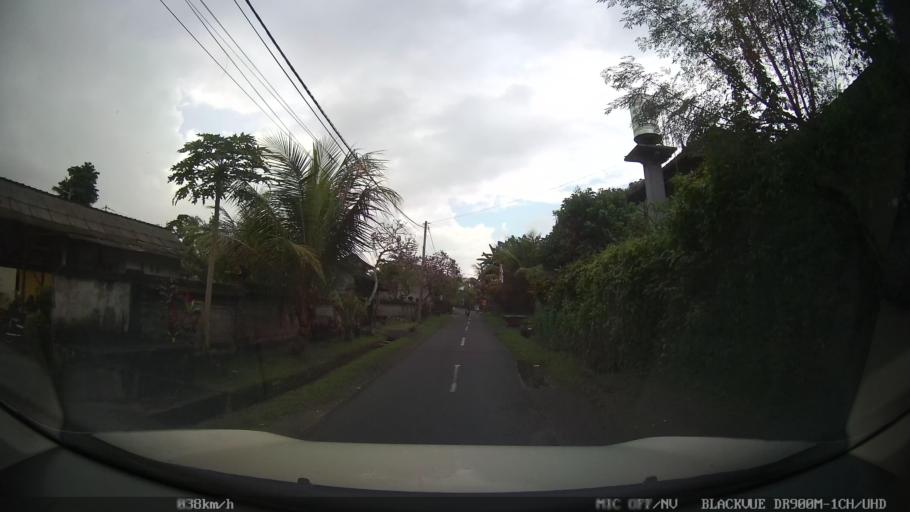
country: ID
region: Bali
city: Banjar Tebongkang
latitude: -8.5282
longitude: 115.2371
